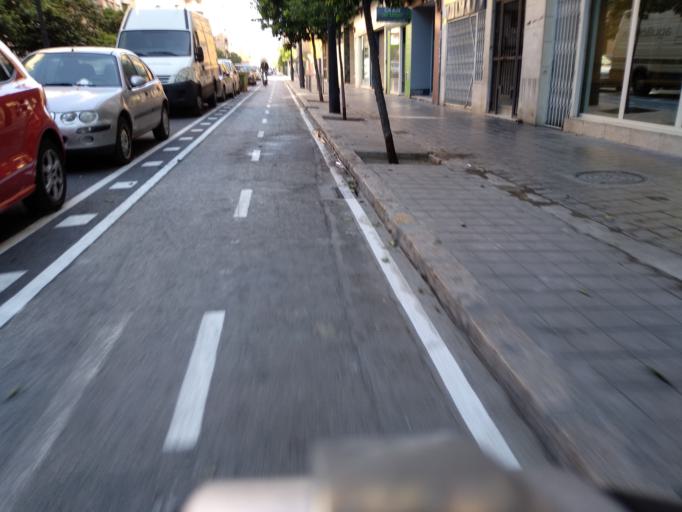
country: ES
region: Valencia
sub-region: Provincia de Valencia
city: Tavernes Blanques
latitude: 39.4889
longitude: -0.3762
